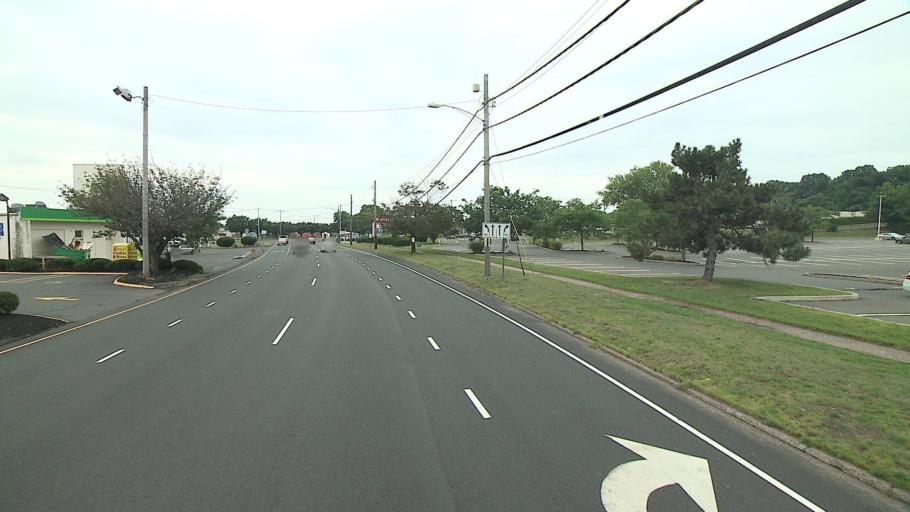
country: US
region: Connecticut
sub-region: New Haven County
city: Hamden
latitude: 41.3758
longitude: -72.9159
